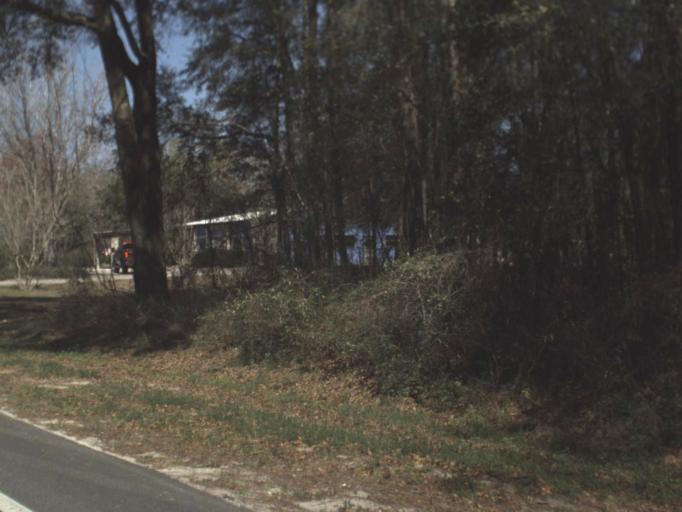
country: US
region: Florida
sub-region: Leon County
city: Woodville
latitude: 30.3001
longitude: -84.2445
